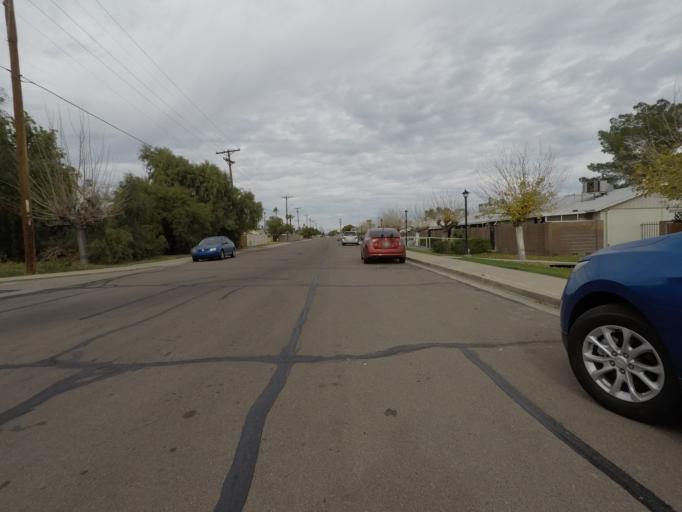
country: US
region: Arizona
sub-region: Maricopa County
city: Tempe Junction
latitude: 33.4562
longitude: -111.9307
